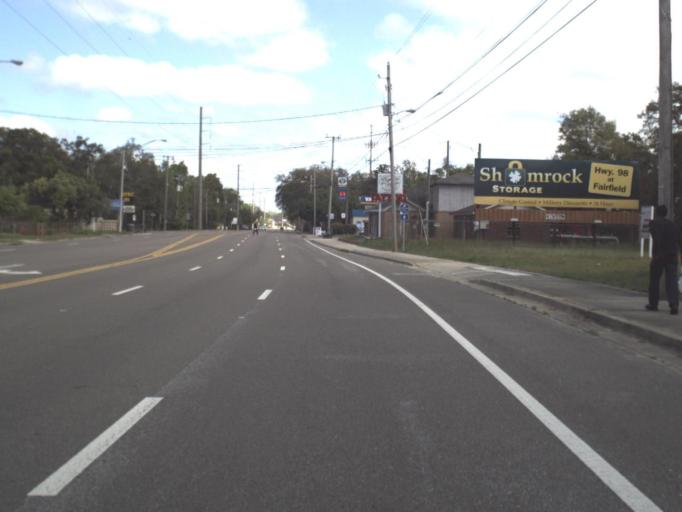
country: US
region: Florida
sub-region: Escambia County
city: Warrington
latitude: 30.3749
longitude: -87.2755
